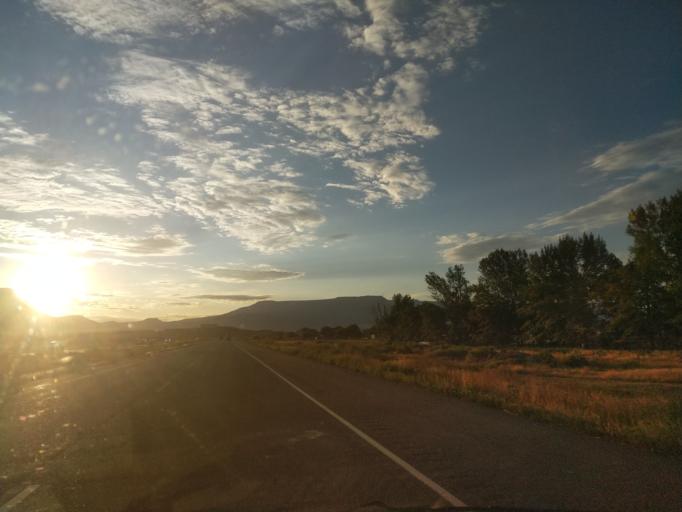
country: US
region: Colorado
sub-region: Mesa County
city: Fruitvale
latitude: 39.1049
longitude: -108.4808
